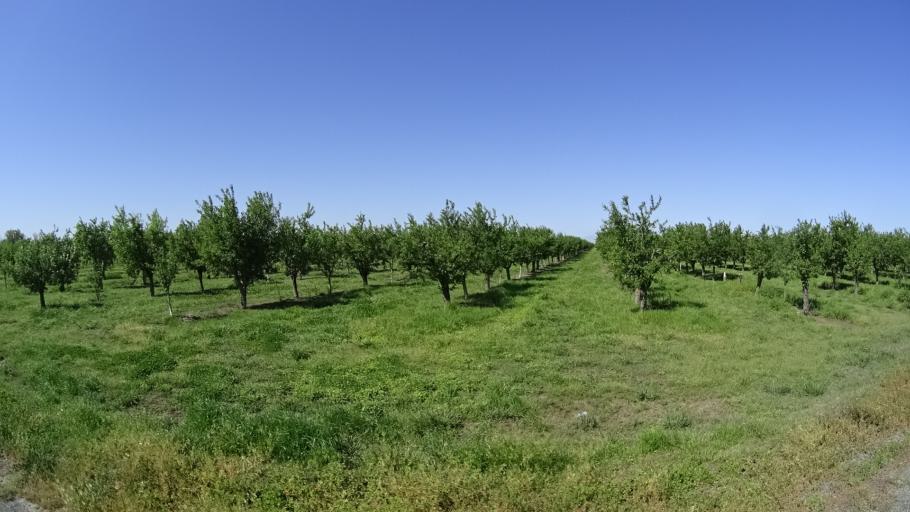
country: US
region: California
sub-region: Glenn County
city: Hamilton City
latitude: 39.7343
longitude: -122.0157
